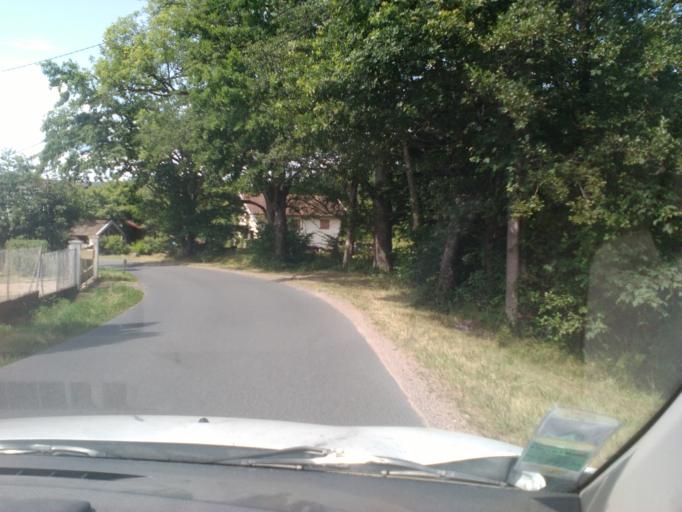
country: FR
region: Lorraine
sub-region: Departement des Vosges
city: Bruyeres
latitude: 48.1429
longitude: 6.6993
